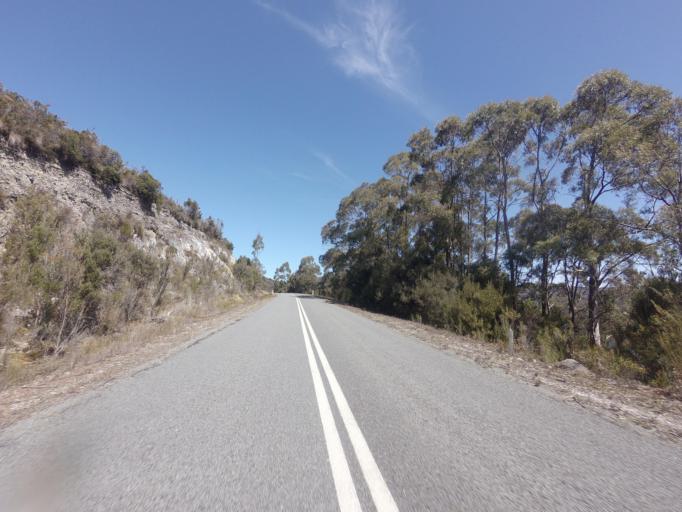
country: AU
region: Tasmania
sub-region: Huon Valley
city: Geeveston
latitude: -42.8255
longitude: 146.1251
